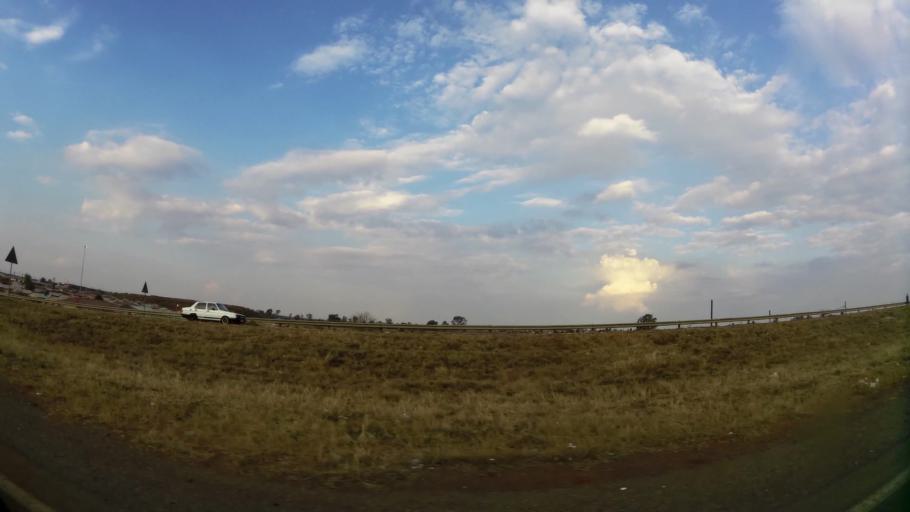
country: ZA
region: Gauteng
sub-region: Sedibeng District Municipality
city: Vanderbijlpark
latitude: -26.6046
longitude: 27.8172
